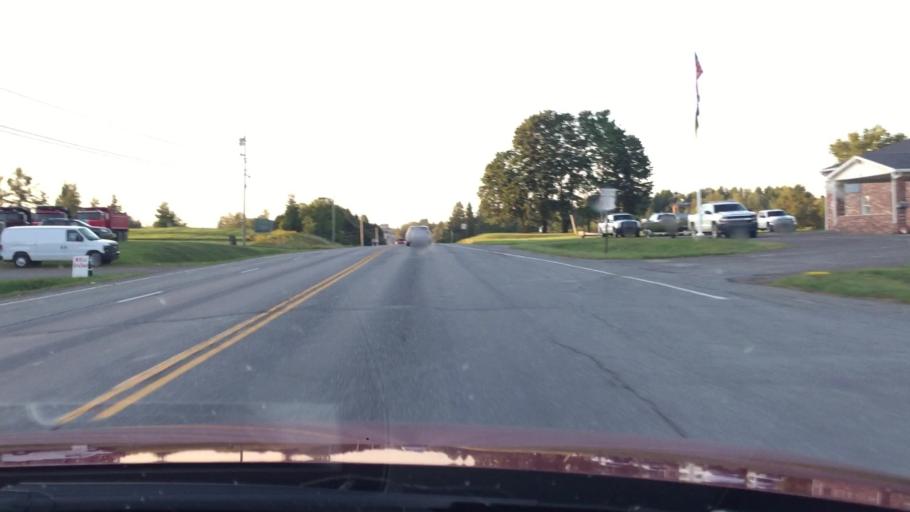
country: US
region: Maine
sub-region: Aroostook County
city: Houlton
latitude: 46.1655
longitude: -67.8405
